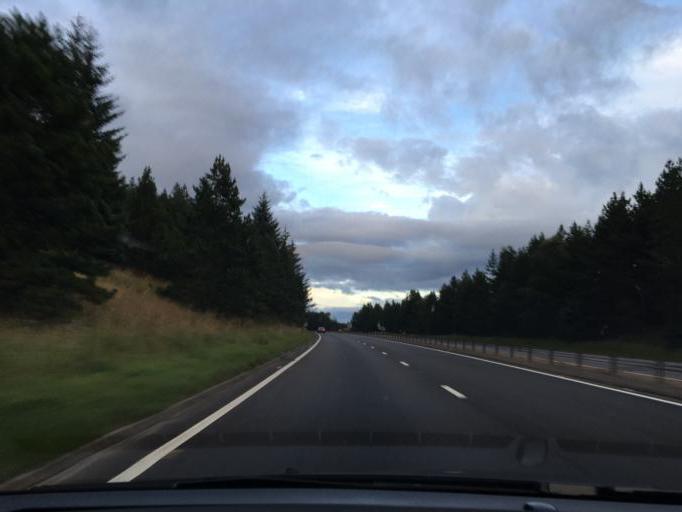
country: GB
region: Scotland
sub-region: Highland
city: Inverness
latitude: 57.3864
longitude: -4.1144
